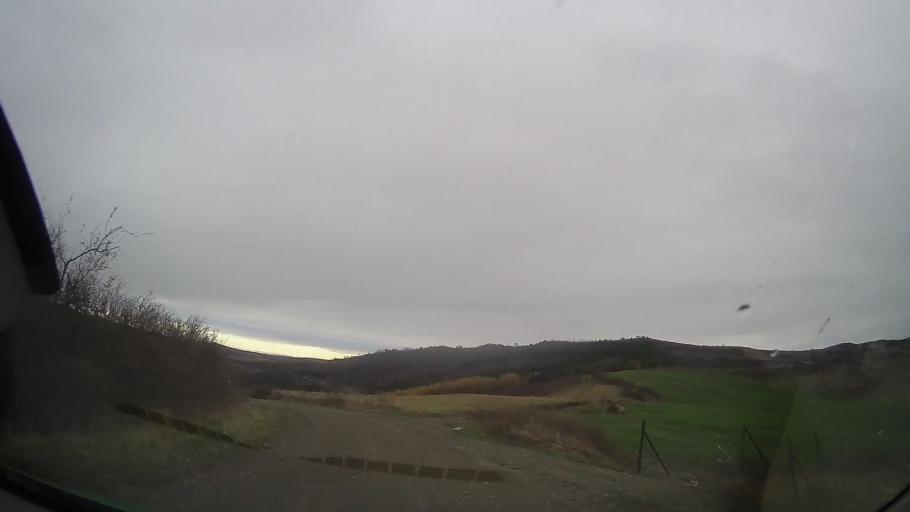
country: RO
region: Mures
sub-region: Comuna Bala
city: Bala
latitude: 46.6749
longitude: 24.4842
